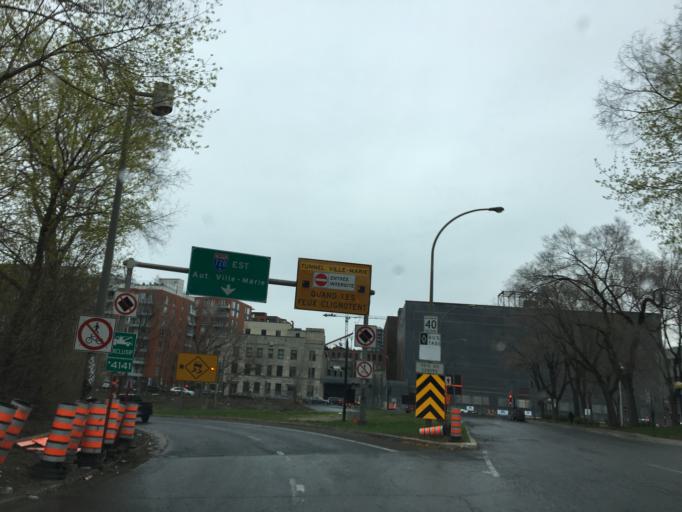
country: CA
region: Quebec
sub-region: Montreal
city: Montreal
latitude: 45.4966
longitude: -73.5640
